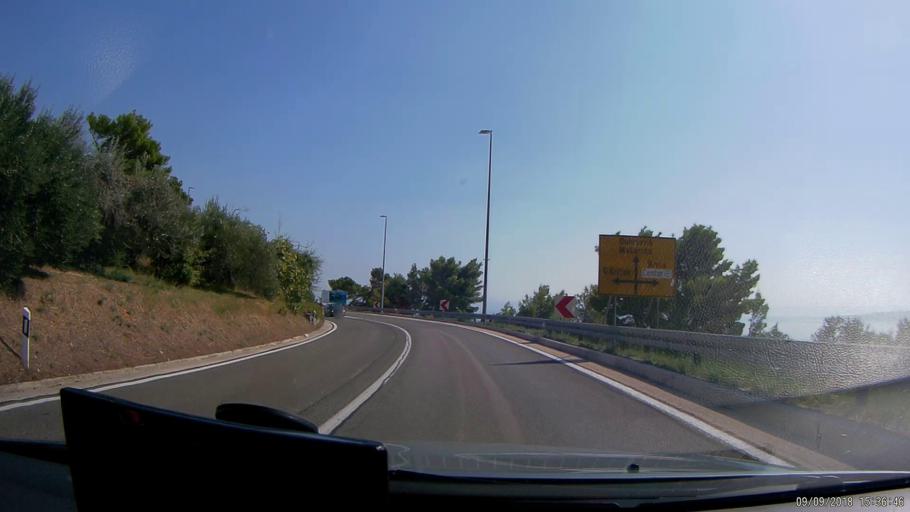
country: HR
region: Splitsko-Dalmatinska
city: Donja Brela
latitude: 43.3759
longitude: 16.9236
